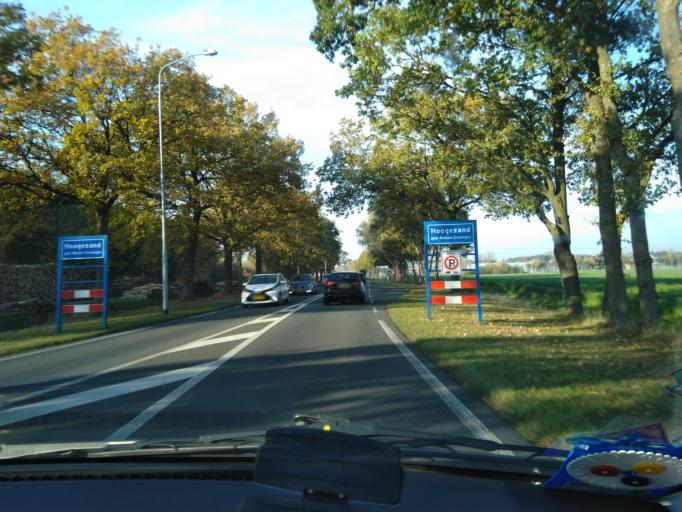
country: NL
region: Groningen
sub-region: Gemeente Hoogezand-Sappemeer
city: Hoogezand
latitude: 53.1457
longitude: 6.7657
